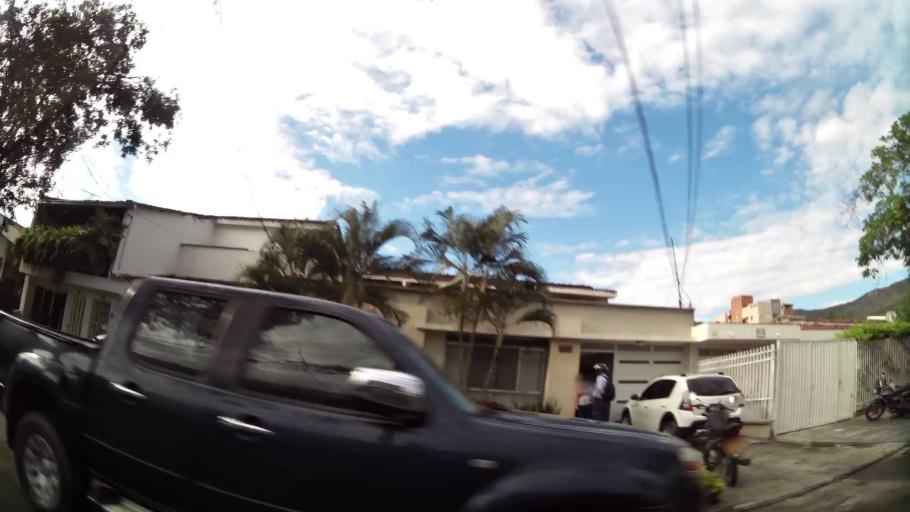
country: CO
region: Valle del Cauca
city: Cali
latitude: 3.4803
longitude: -76.5233
